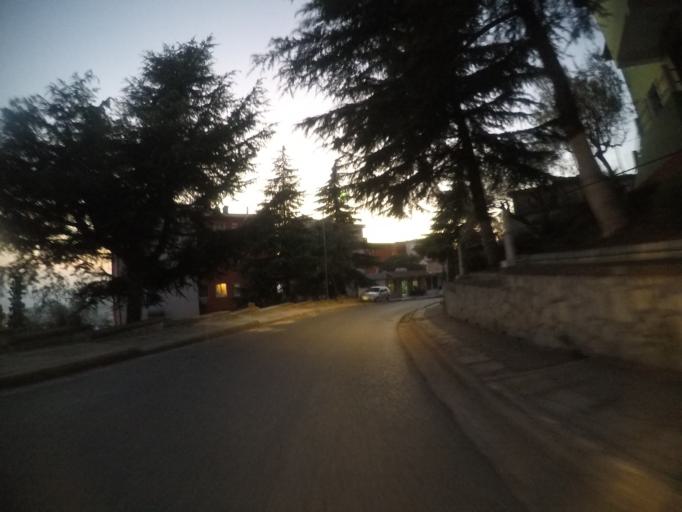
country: AL
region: Durres
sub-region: Rrethi i Krujes
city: Kruje
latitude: 41.5130
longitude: 19.7911
